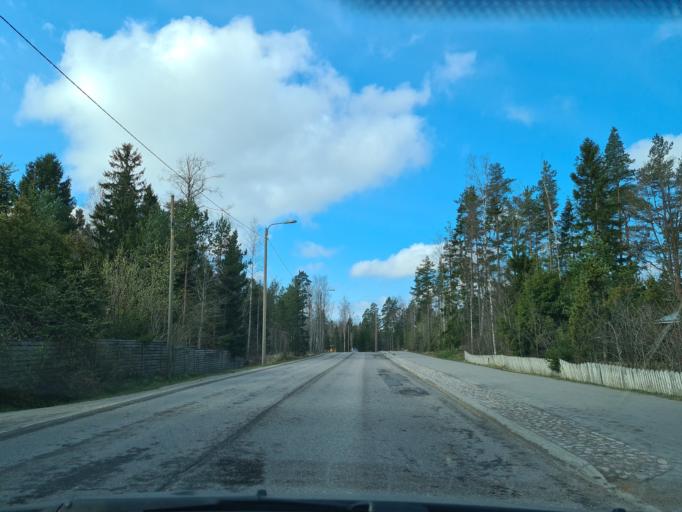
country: FI
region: Uusimaa
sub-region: Helsinki
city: Kirkkonummi
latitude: 60.0834
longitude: 24.4038
